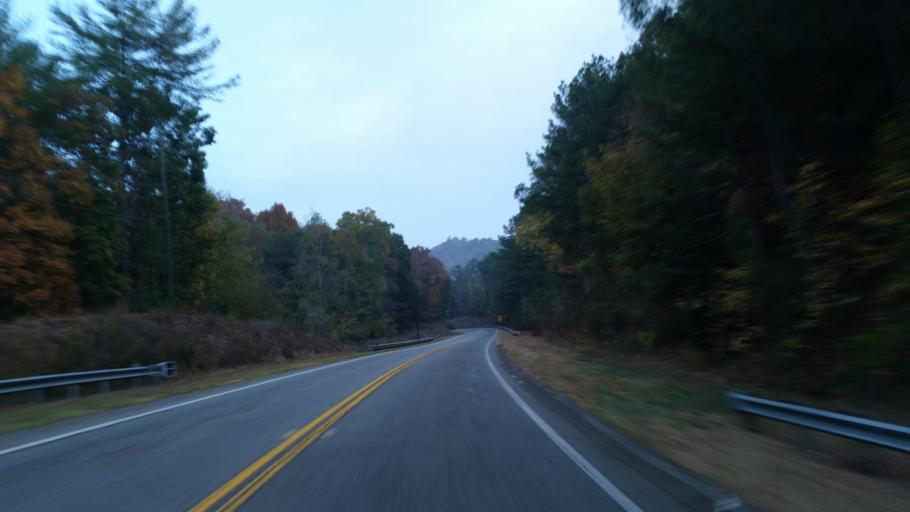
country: US
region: Georgia
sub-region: Murray County
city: Chatsworth
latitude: 34.5907
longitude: -84.6830
